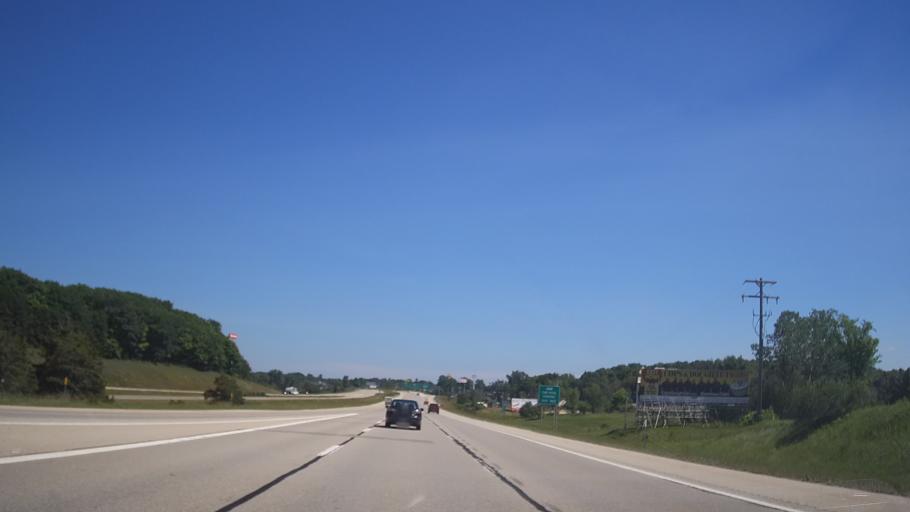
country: US
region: Michigan
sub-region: Clare County
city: Clare
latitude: 43.8479
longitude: -84.7751
